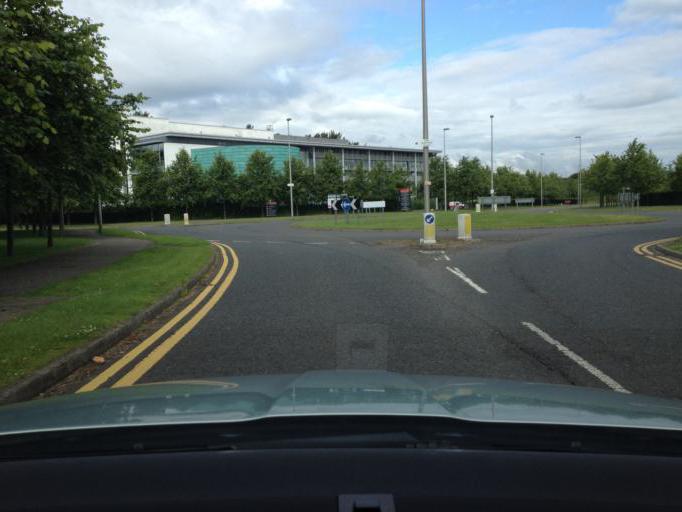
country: GB
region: Scotland
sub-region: West Lothian
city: West Calder
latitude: 55.8729
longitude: -3.5456
